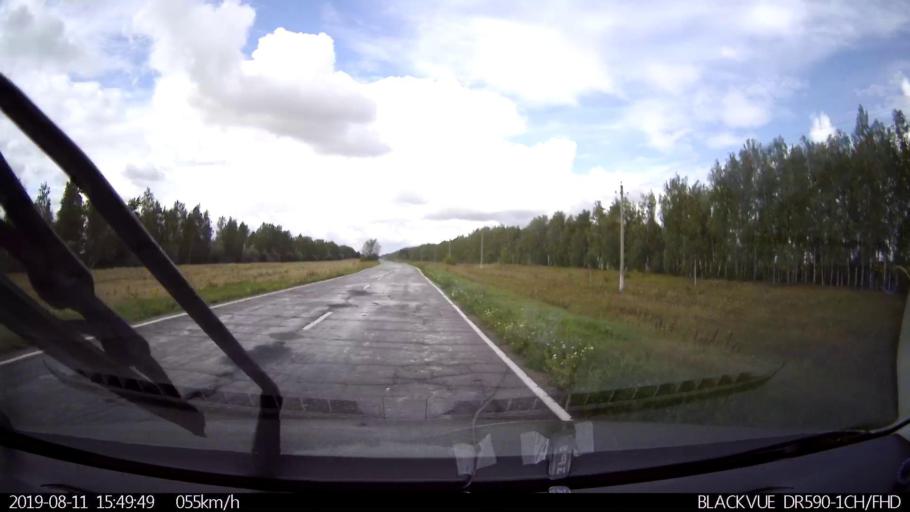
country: RU
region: Ulyanovsk
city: Ignatovka
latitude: 53.9074
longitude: 47.6555
